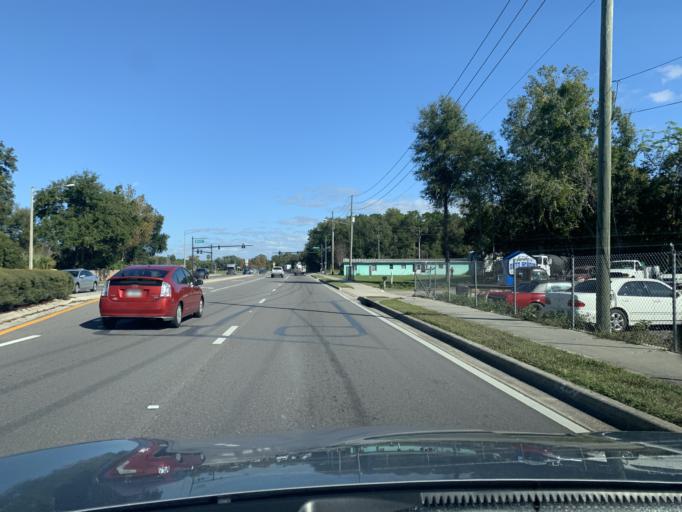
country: US
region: Florida
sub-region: Seminole County
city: Forest City
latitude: 28.6472
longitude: -81.4726
